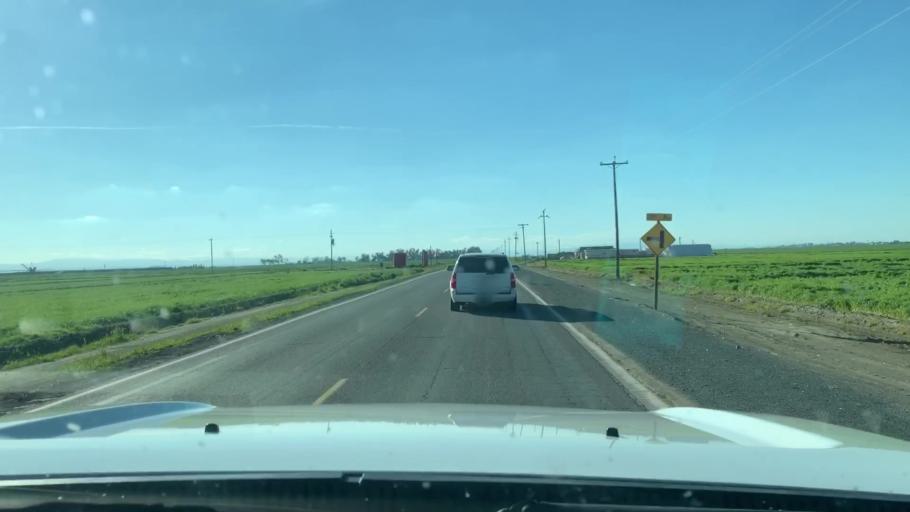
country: US
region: California
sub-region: Kings County
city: Home Garden
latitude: 36.2111
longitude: -119.6882
